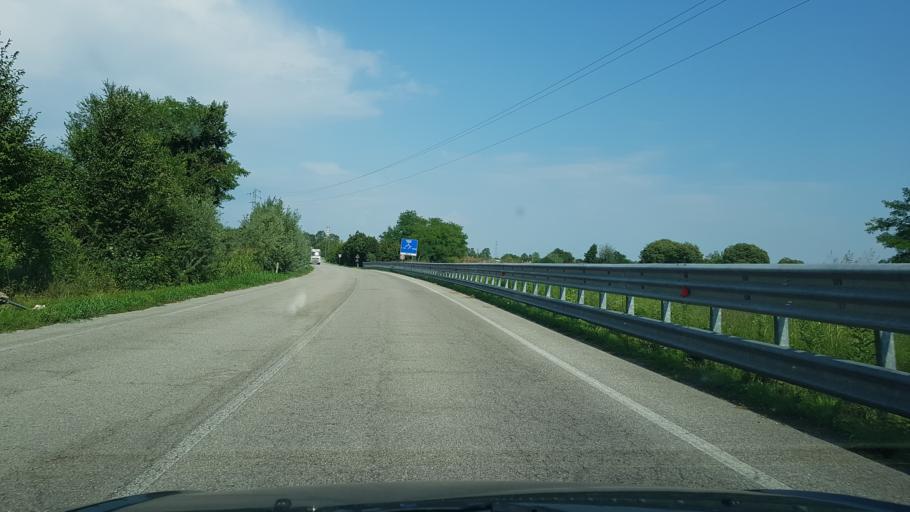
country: IT
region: Friuli Venezia Giulia
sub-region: Provincia di Pordenone
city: San Quirino
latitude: 46.0524
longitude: 12.6882
